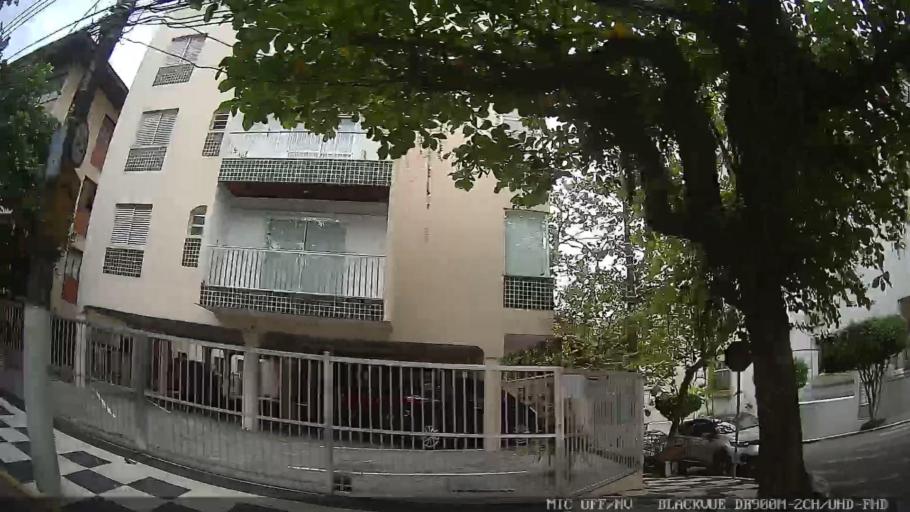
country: BR
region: Sao Paulo
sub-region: Guaruja
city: Guaruja
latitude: -24.0122
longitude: -46.2727
